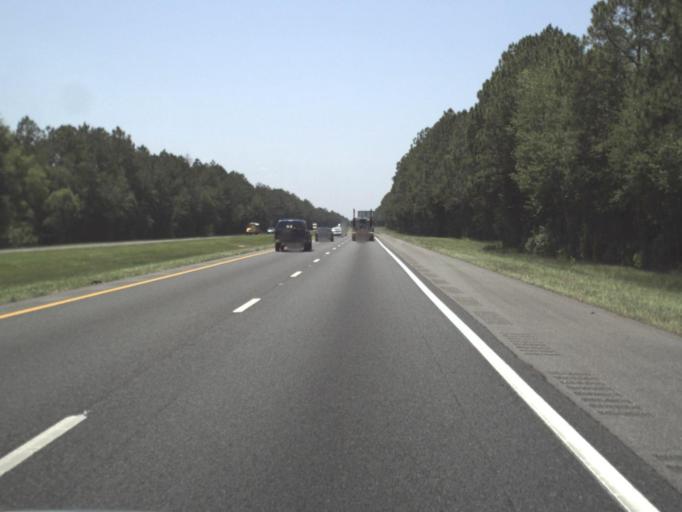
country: US
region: Florida
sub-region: Baker County
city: Macclenny
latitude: 30.2500
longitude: -82.2183
